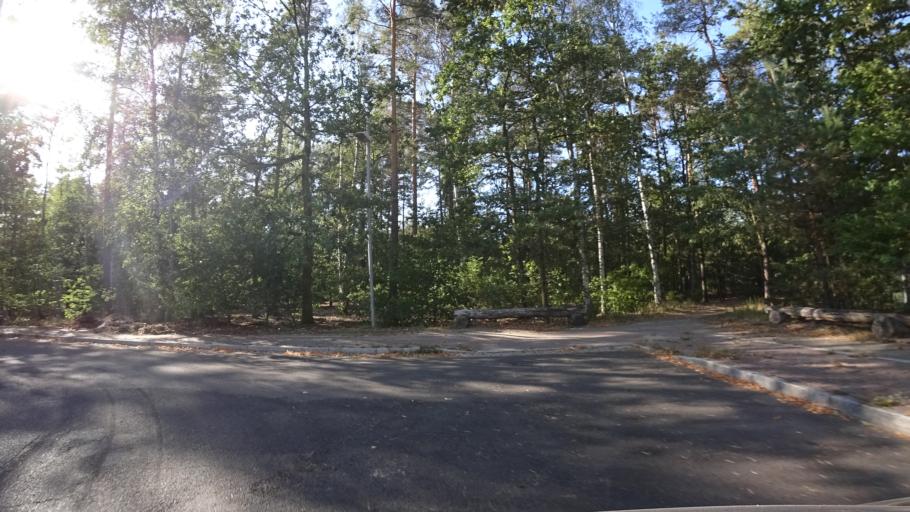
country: DE
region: Berlin
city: Nikolassee
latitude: 52.4112
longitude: 13.1944
